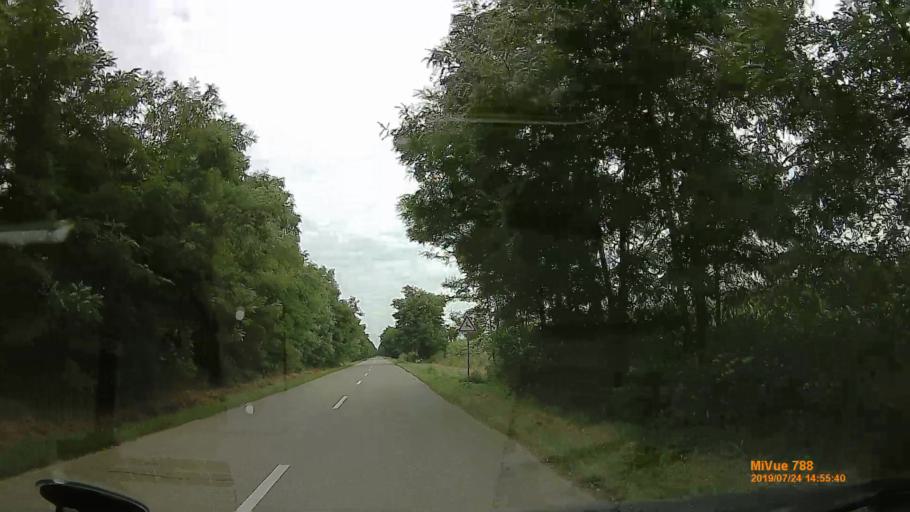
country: HU
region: Szabolcs-Szatmar-Bereg
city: Aranyosapati
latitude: 48.2534
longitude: 22.3149
